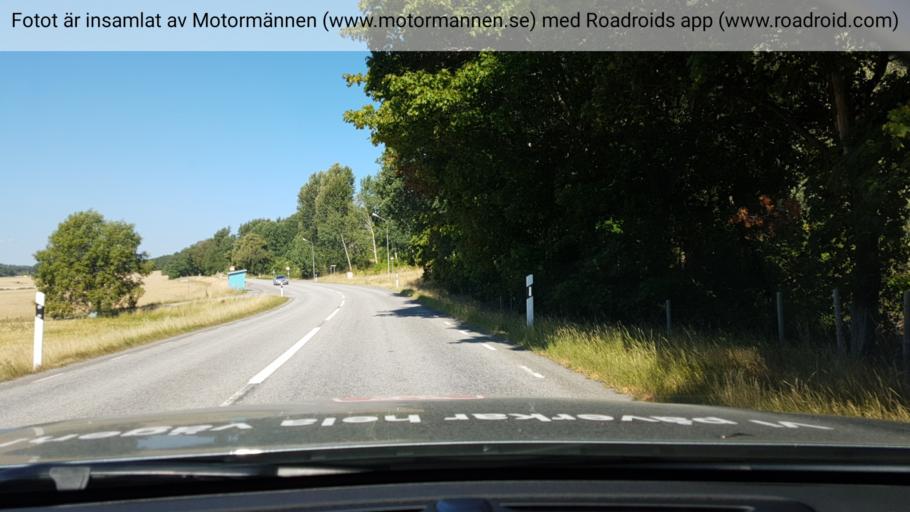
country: SE
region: Stockholm
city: Stenhamra
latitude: 59.2840
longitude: 17.7287
